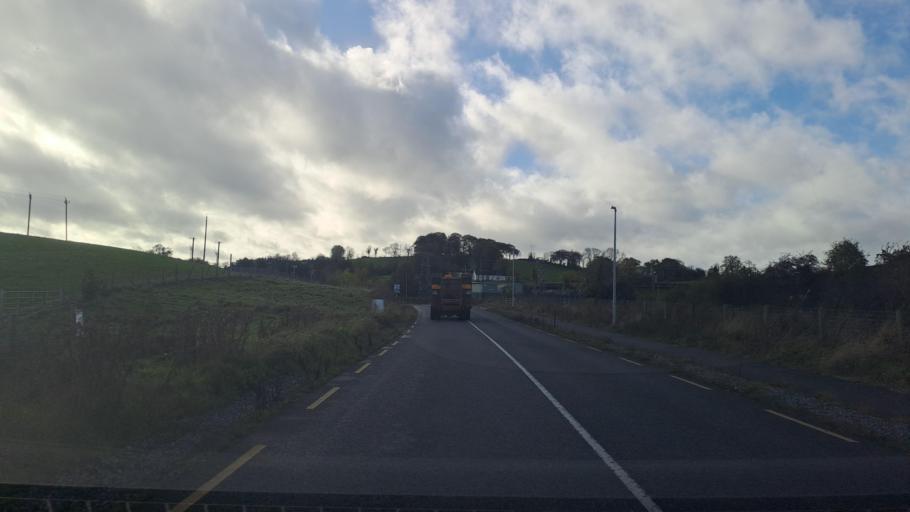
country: IE
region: Ulster
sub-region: County Monaghan
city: Monaghan
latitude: 54.1221
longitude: -6.9062
